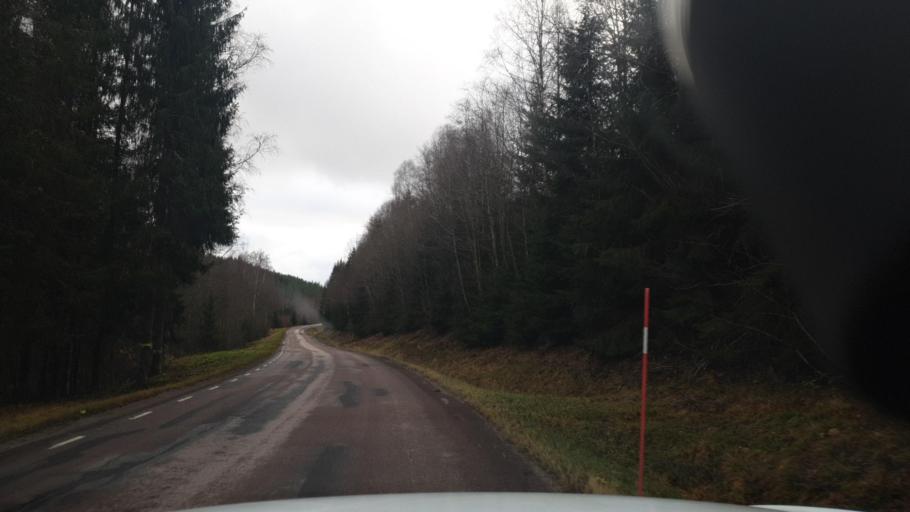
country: SE
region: Vaermland
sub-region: Arvika Kommun
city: Arvika
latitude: 59.7167
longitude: 12.7962
